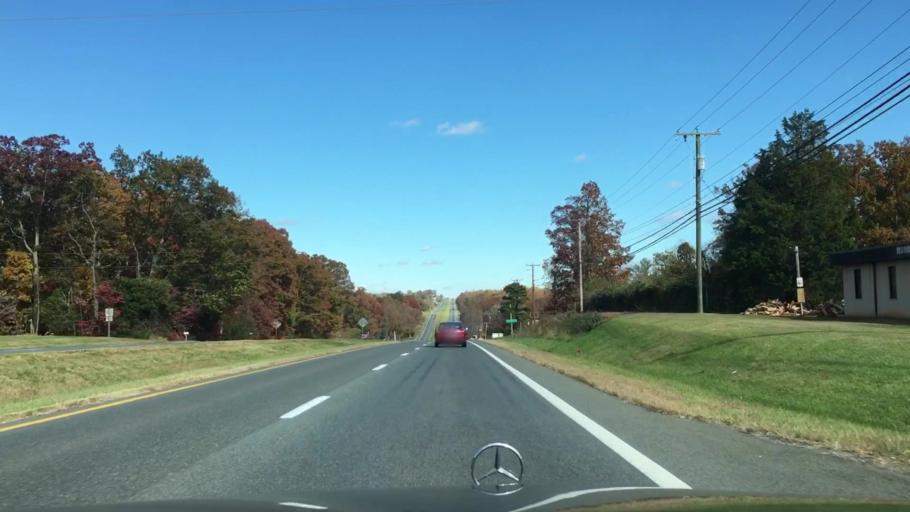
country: US
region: Virginia
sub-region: Campbell County
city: Rustburg
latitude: 37.2572
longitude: -79.1839
